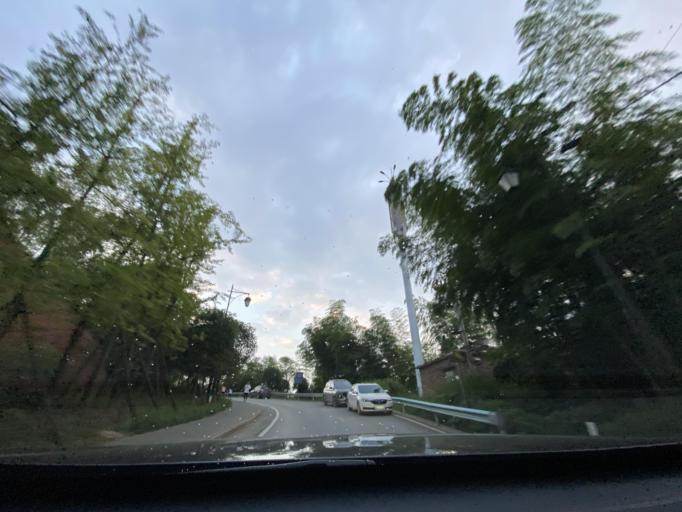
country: CN
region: Guizhou Sheng
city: Changqi
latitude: 28.5399
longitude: 105.9870
